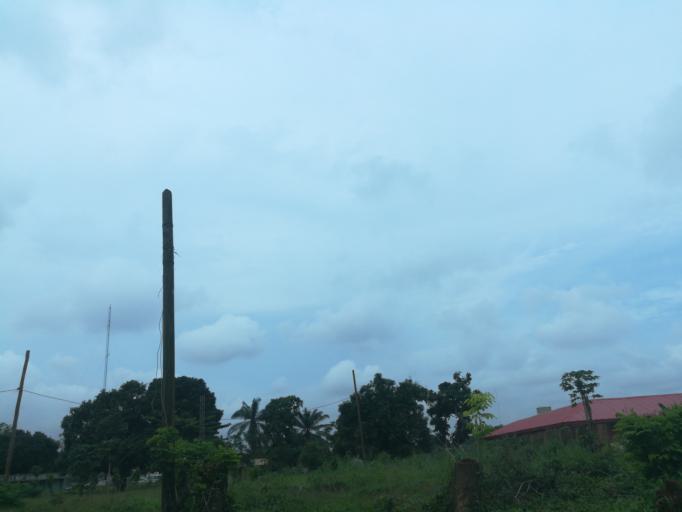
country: NG
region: Lagos
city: Oshodi
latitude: 6.5663
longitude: 3.3610
